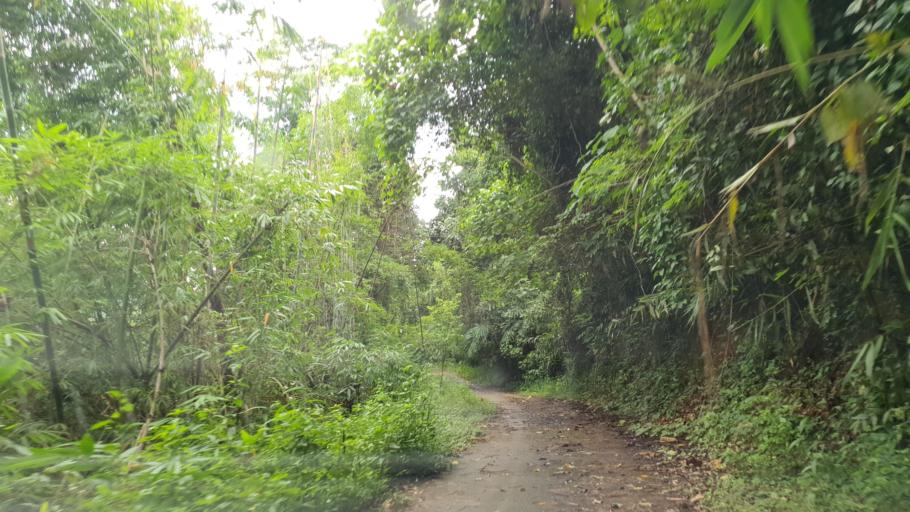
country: TH
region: Chiang Mai
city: Mae On
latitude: 18.9278
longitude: 99.3096
